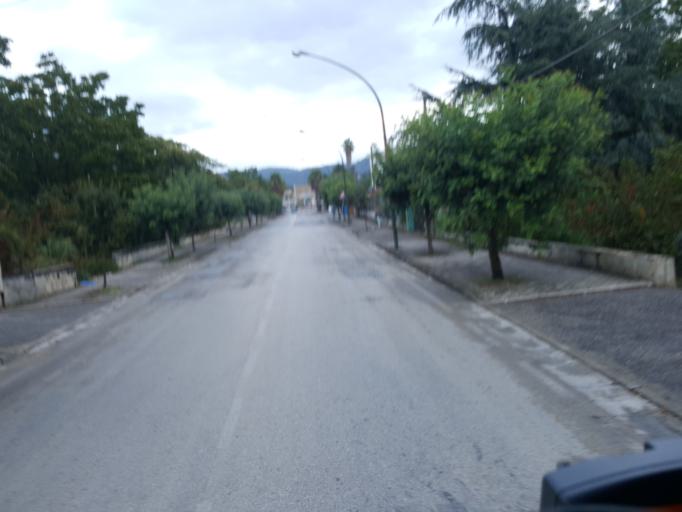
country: IT
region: Campania
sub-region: Provincia di Napoli
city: Palma Campania
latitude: 40.8754
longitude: 14.5499
